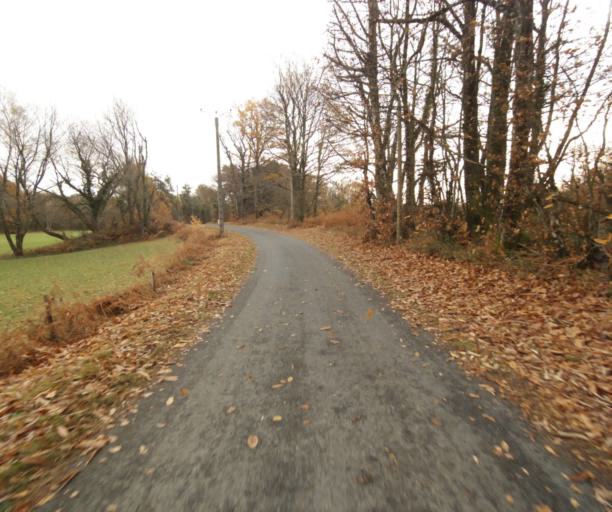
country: FR
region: Limousin
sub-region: Departement de la Correze
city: Sainte-Fortunade
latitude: 45.1906
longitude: 1.7536
